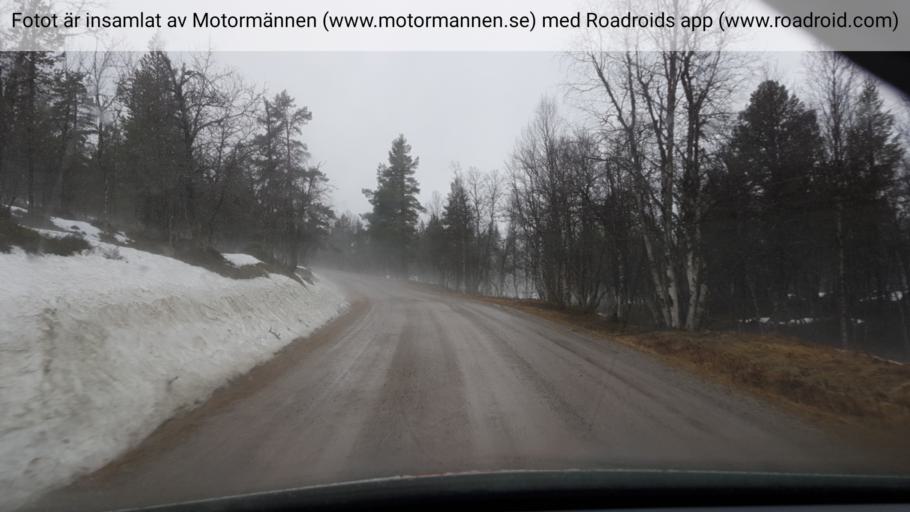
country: NO
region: Hedmark
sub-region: Engerdal
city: Engerdal
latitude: 62.1441
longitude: 12.9511
